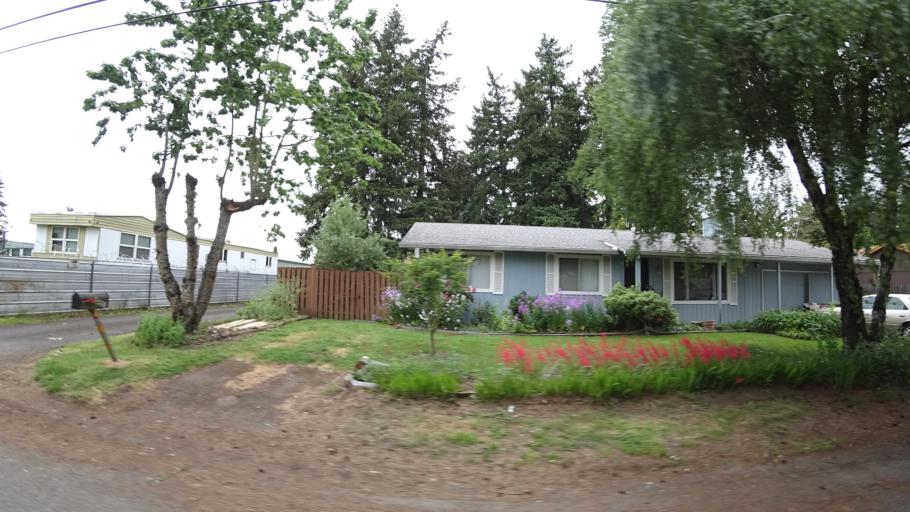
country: US
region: Oregon
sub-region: Multnomah County
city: Lents
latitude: 45.5050
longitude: -122.5157
